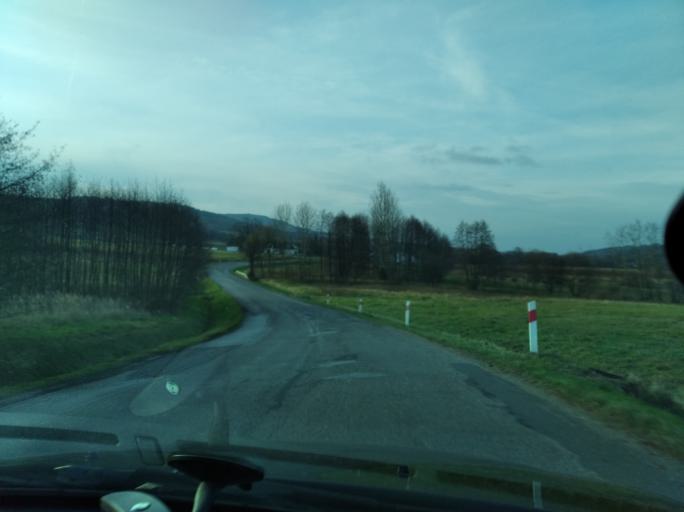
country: PL
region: Subcarpathian Voivodeship
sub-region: Powiat strzyzowski
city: Jawornik
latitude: 49.8033
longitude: 21.8627
